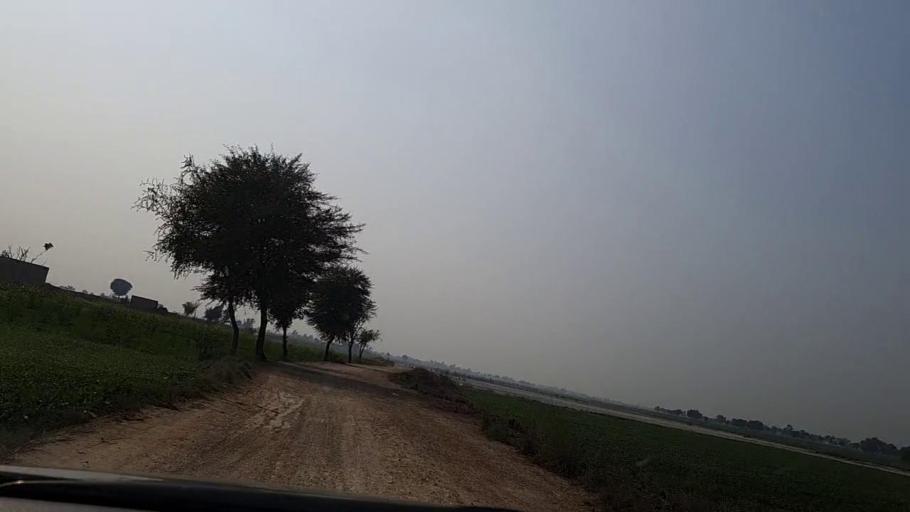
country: PK
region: Sindh
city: Sakrand
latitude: 26.1478
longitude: 68.2371
